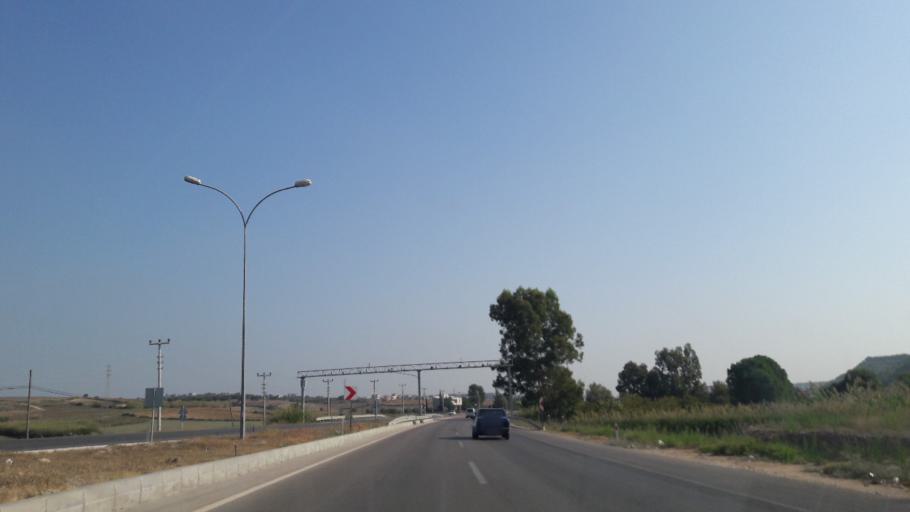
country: TR
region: Adana
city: Yuregir
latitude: 37.0626
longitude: 35.4455
